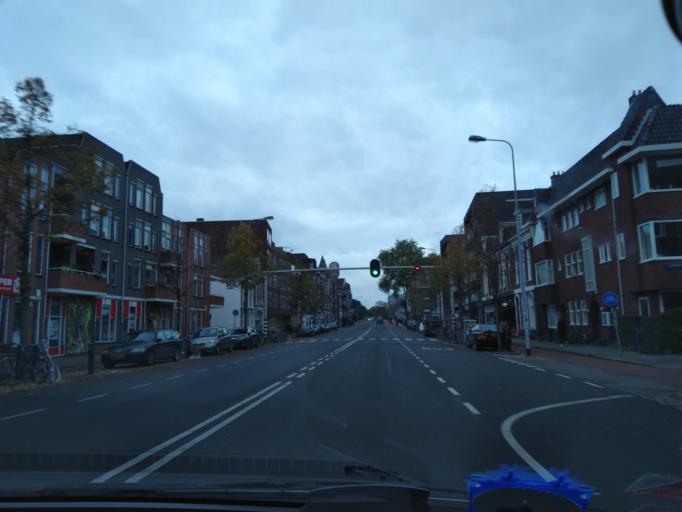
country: NL
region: Groningen
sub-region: Gemeente Groningen
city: Groningen
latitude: 53.2088
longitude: 6.5724
